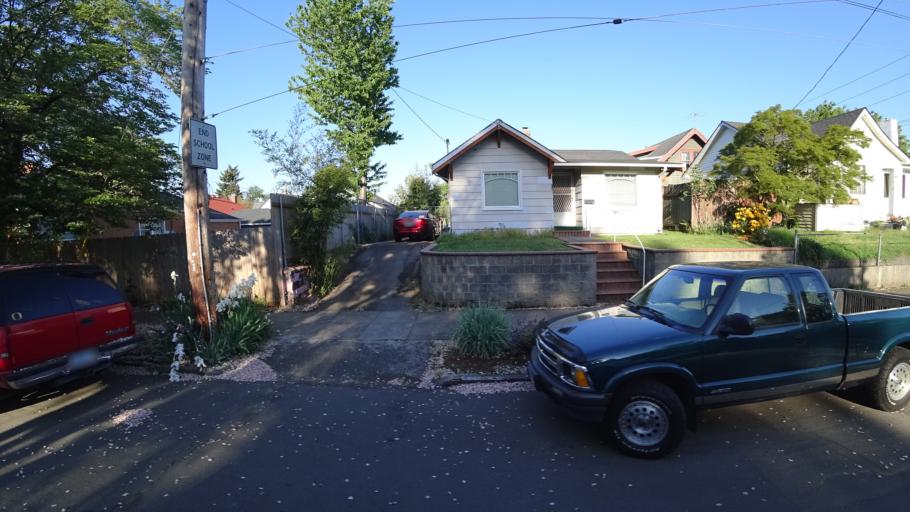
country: US
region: Oregon
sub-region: Multnomah County
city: Portland
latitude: 45.5587
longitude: -122.6849
